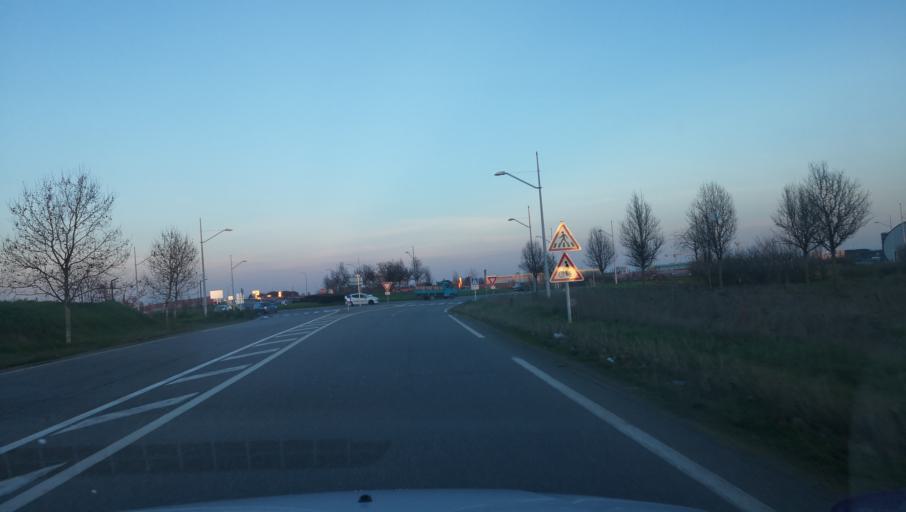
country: FR
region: Midi-Pyrenees
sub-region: Departement de la Haute-Garonne
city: Beauzelle
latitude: 43.6618
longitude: 1.3550
